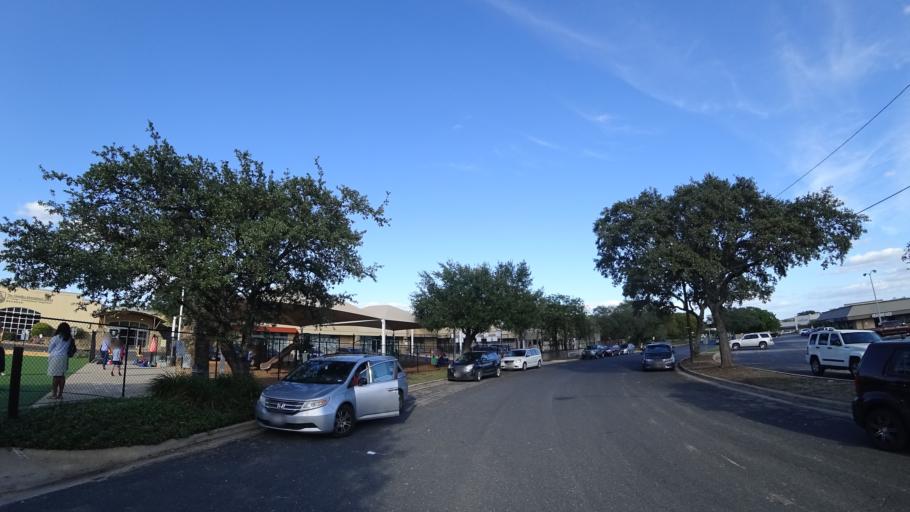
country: US
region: Texas
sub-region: Williamson County
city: Jollyville
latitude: 30.3626
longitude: -97.7423
